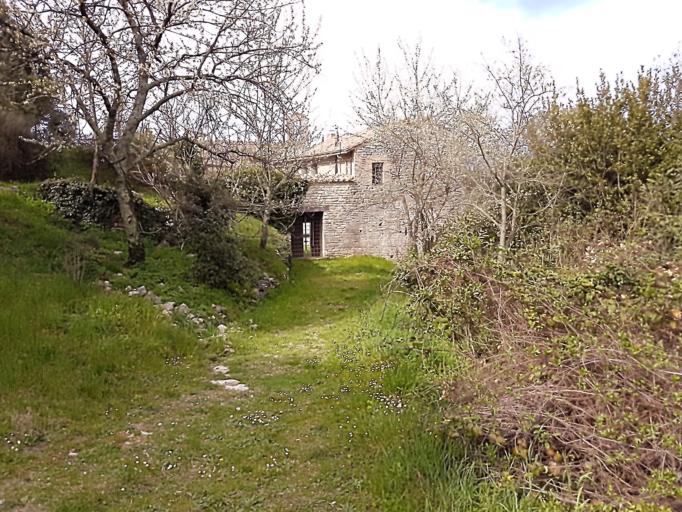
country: IT
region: Umbria
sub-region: Provincia di Perugia
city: Corciano
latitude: 43.1322
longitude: 12.3062
